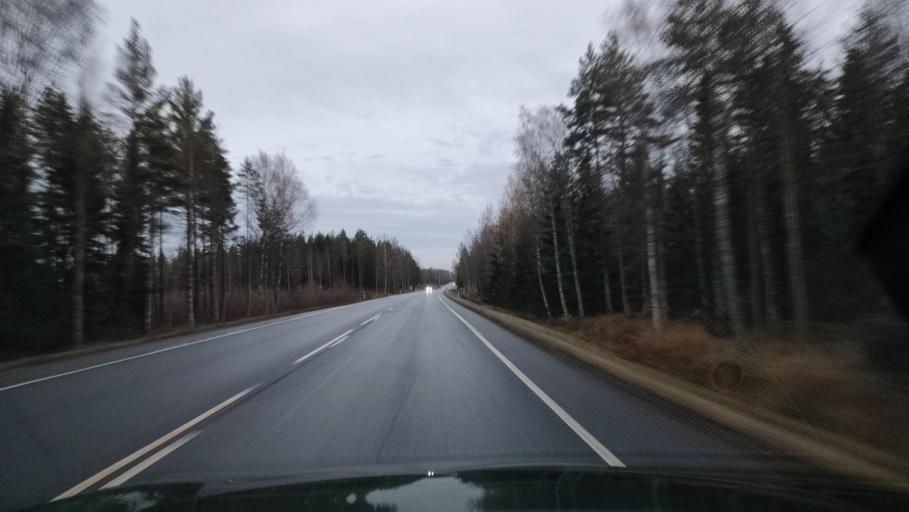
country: FI
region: Ostrobothnia
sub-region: Vaasa
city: Ristinummi
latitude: 63.0119
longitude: 21.7614
